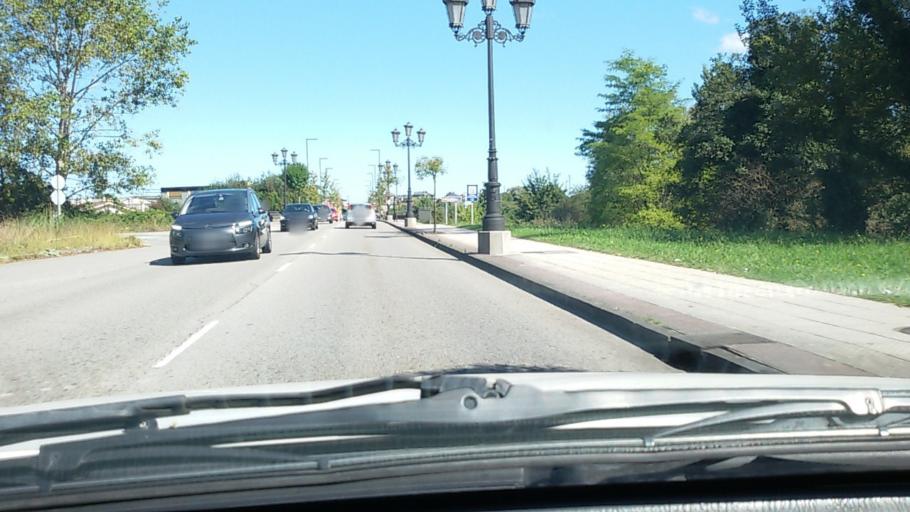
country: ES
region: Asturias
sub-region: Province of Asturias
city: Lugones
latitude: 43.3929
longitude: -5.8177
